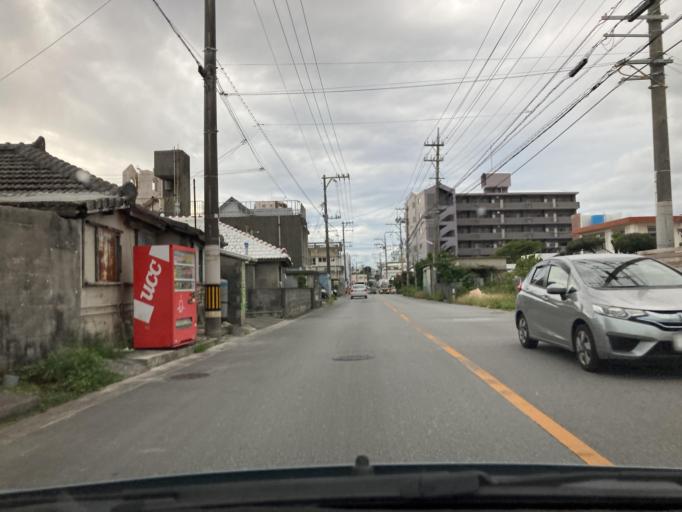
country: JP
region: Okinawa
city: Ginowan
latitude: 26.2695
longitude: 127.7384
